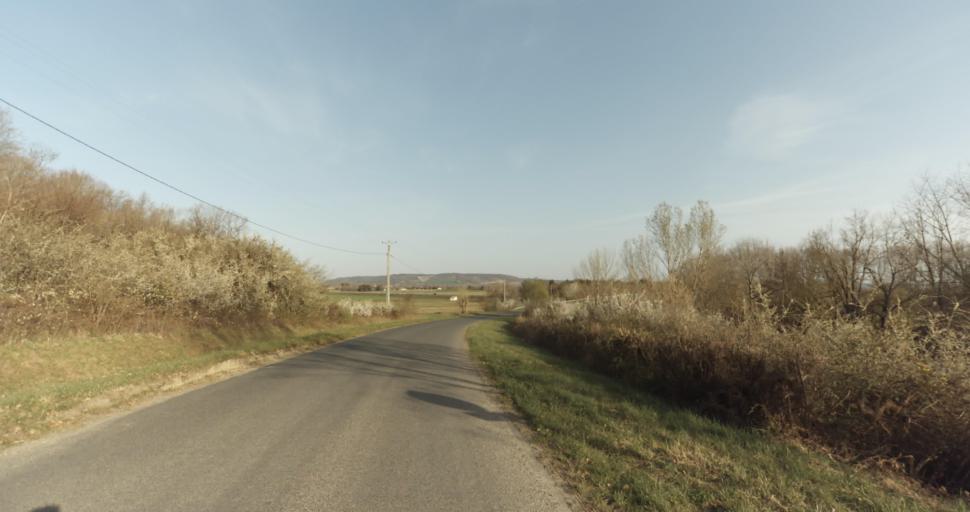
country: FR
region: Midi-Pyrenees
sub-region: Departement du Tarn
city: Saint-Sulpice-la-Pointe
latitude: 43.7507
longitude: 1.6866
